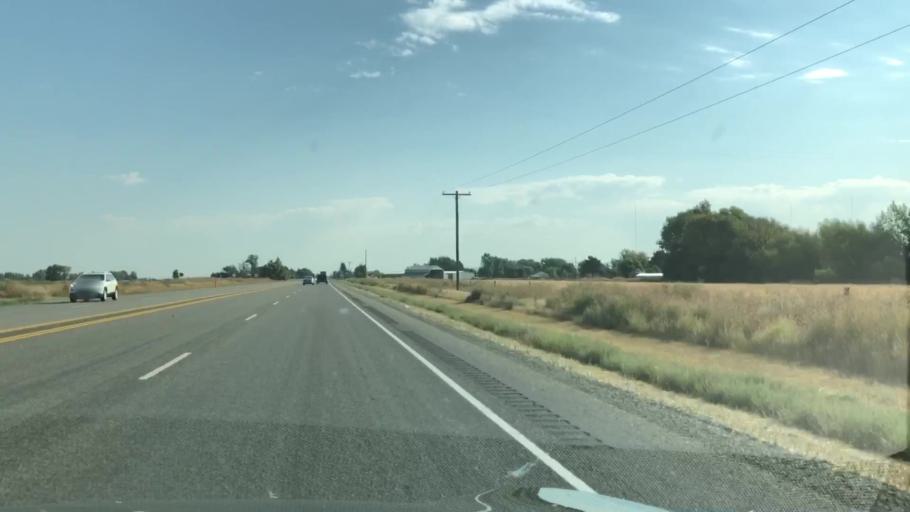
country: US
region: Idaho
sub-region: Bonneville County
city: Iona
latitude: 43.5562
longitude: -111.9390
